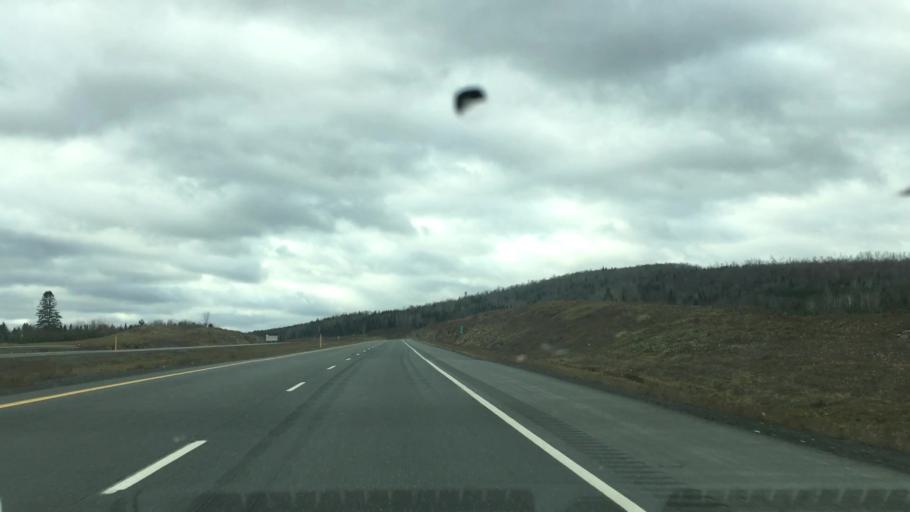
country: US
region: Maine
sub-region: Aroostook County
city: Fort Fairfield
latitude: 46.7309
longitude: -67.7229
